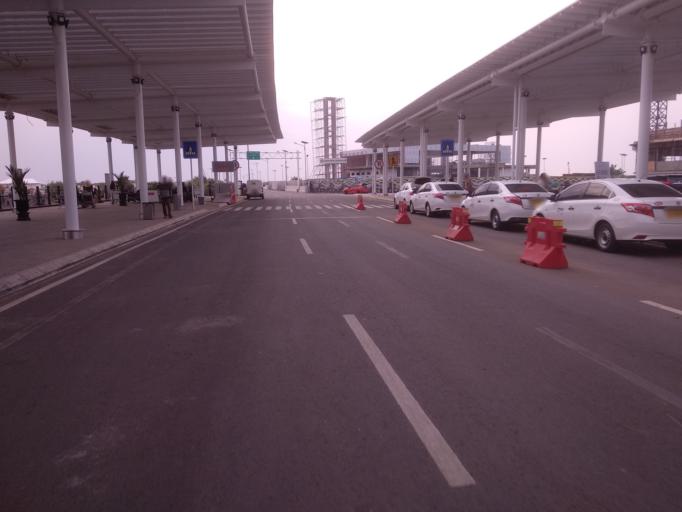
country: ID
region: Central Java
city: Semarang
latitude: -6.9655
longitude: 110.3749
